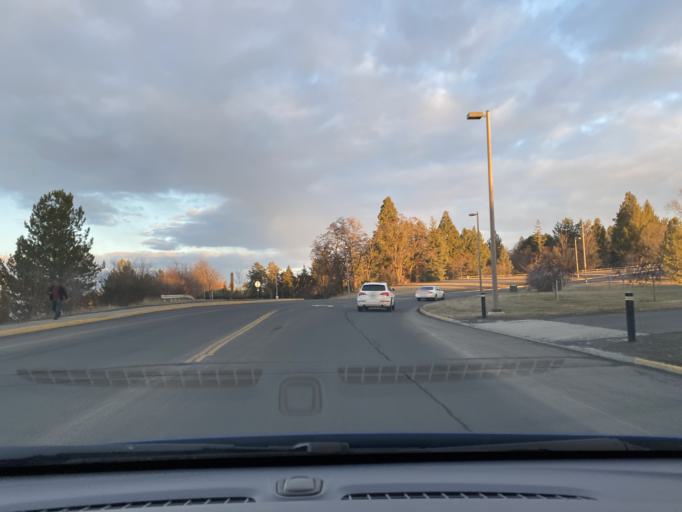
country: US
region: Idaho
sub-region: Latah County
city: Moscow
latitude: 46.7254
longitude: -117.0188
